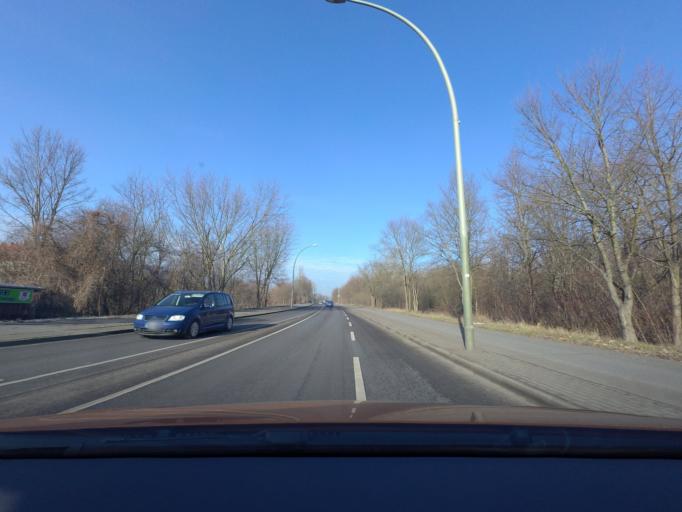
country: DE
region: Berlin
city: Blankenfelde
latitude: 52.6204
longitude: 13.3894
